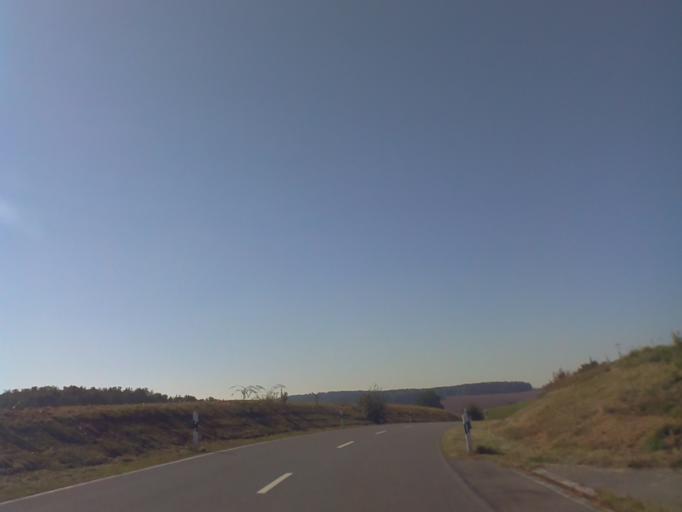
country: DE
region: Thuringia
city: Tautendorf
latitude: 50.8007
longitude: 11.8923
